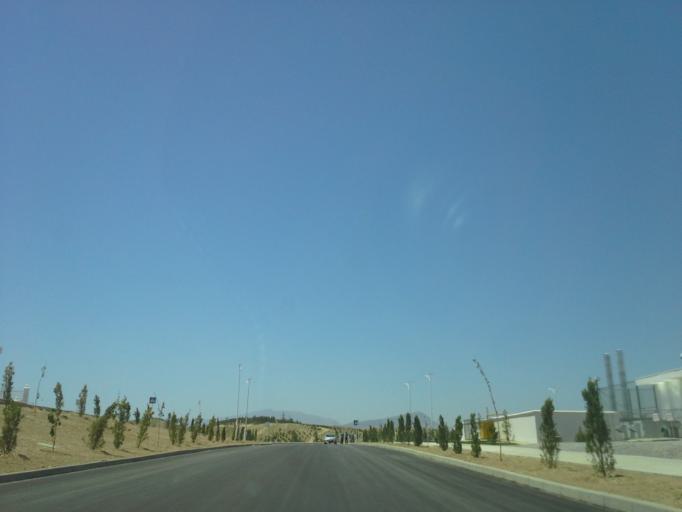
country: TM
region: Ahal
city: Ashgabat
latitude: 37.9396
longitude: 58.3461
